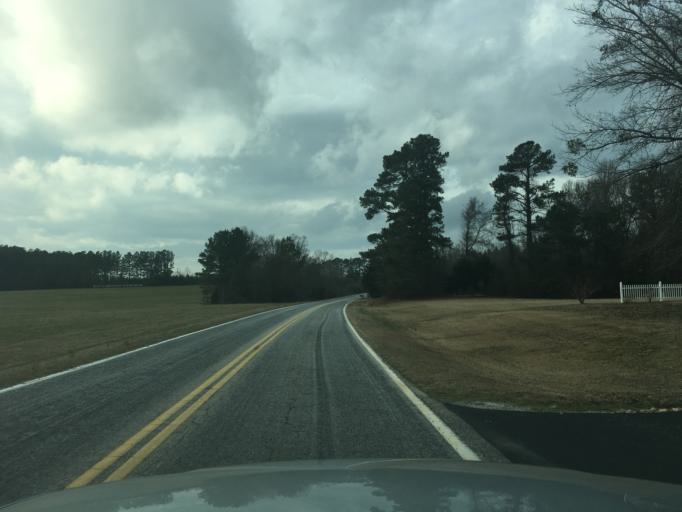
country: US
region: South Carolina
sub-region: Abbeville County
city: Abbeville
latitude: 34.2435
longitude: -82.4089
